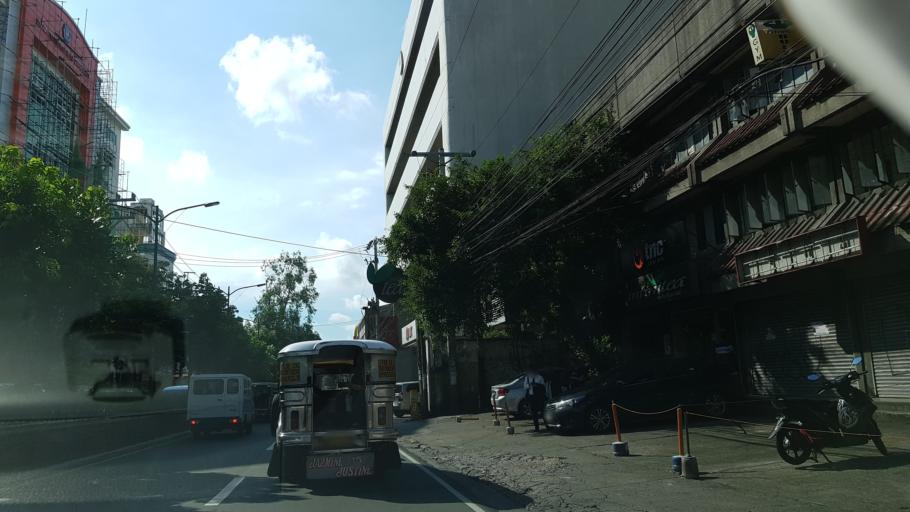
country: PH
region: Metro Manila
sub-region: Mandaluyong
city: Mandaluyong City
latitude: 14.5746
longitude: 121.0431
